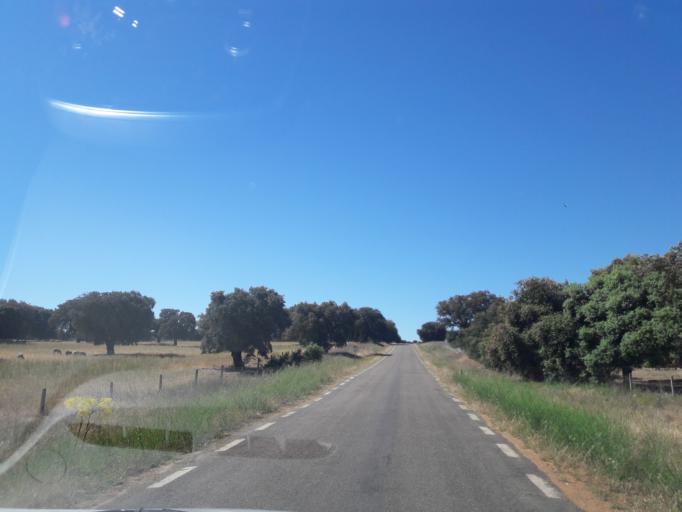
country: ES
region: Castille and Leon
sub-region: Provincia de Salamanca
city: Parada de Arriba
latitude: 41.0115
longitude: -5.8145
